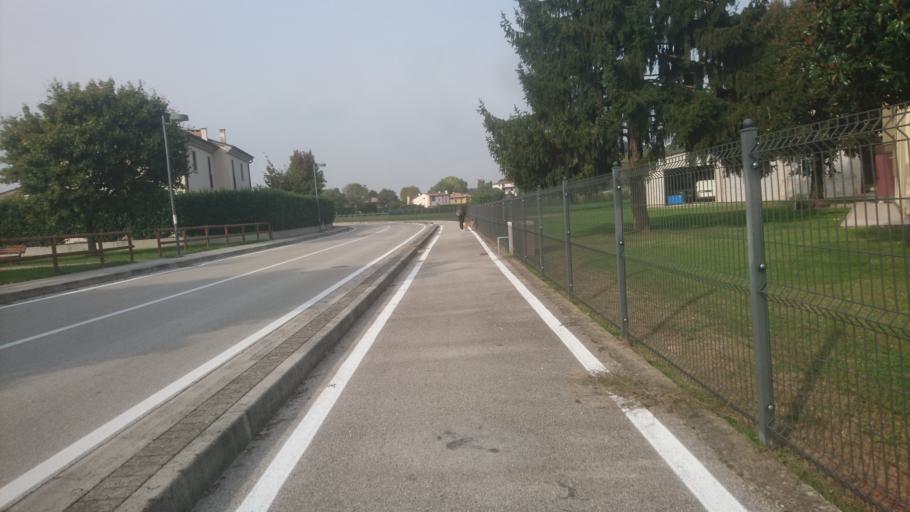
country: IT
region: Veneto
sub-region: Provincia di Vicenza
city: Montegalda
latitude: 45.4511
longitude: 11.6629
